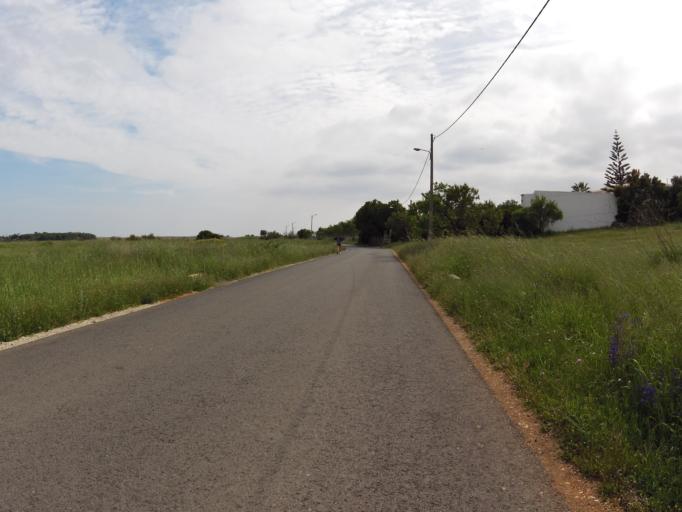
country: PT
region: Faro
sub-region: Silves
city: Armacao de Pera
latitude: 37.1110
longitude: -8.3488
